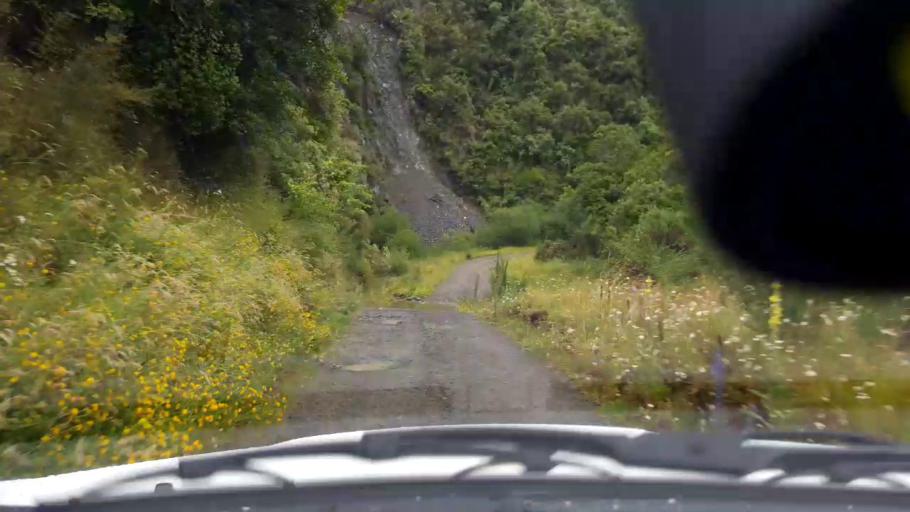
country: NZ
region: Canterbury
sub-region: Timaru District
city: Pleasant Point
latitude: -44.0444
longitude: 171.0184
